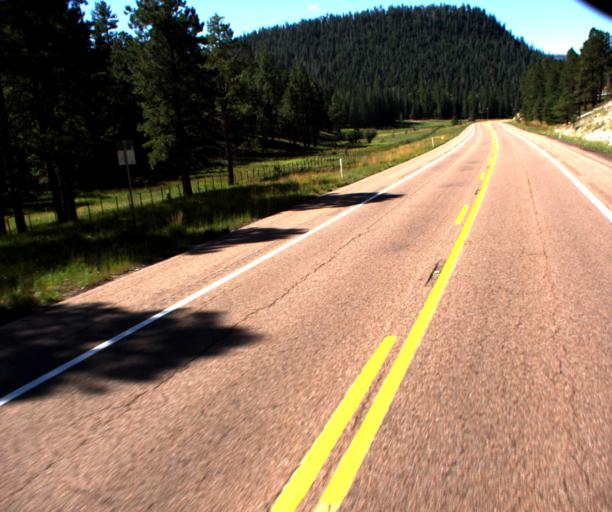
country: US
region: Arizona
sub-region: Apache County
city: Eagar
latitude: 33.8875
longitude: -109.1576
